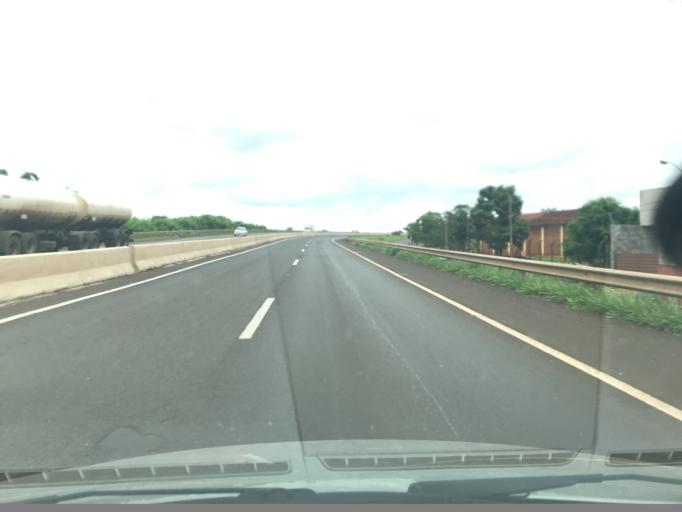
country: BR
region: Parana
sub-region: Maringa
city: Maringa
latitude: -23.3725
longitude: -51.9272
